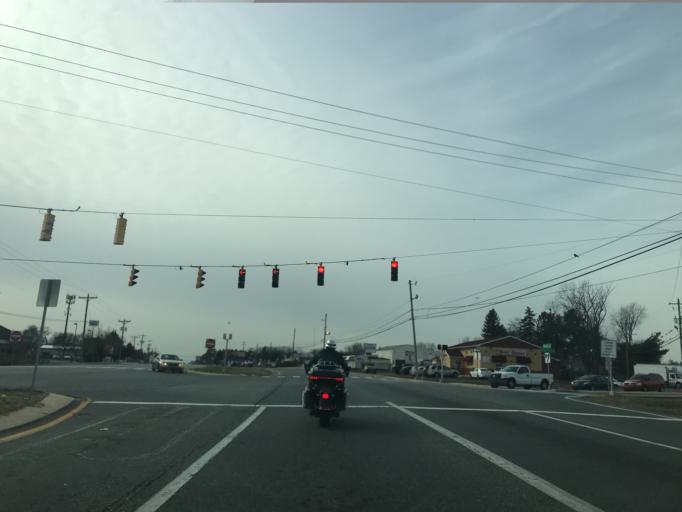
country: US
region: Delaware
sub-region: New Castle County
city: Bear
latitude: 39.6476
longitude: -75.6337
